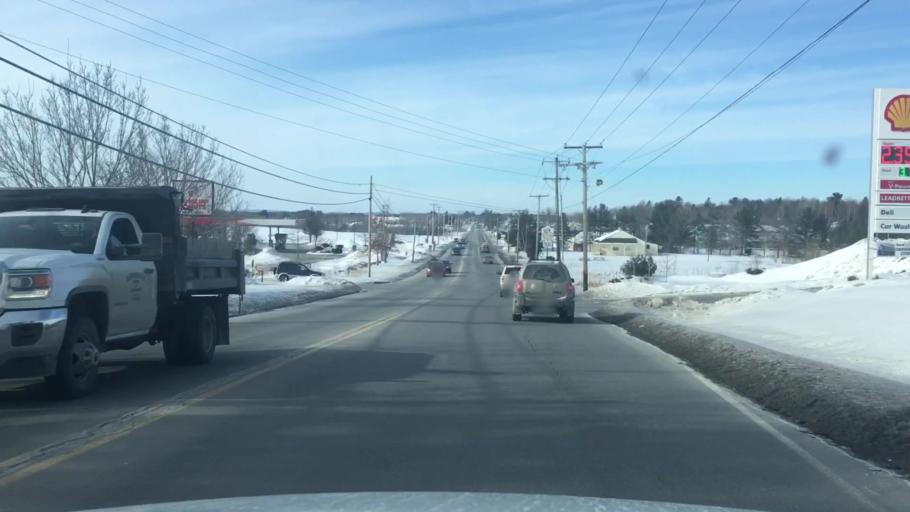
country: US
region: Maine
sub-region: Penobscot County
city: Bangor
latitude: 44.8342
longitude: -68.7896
